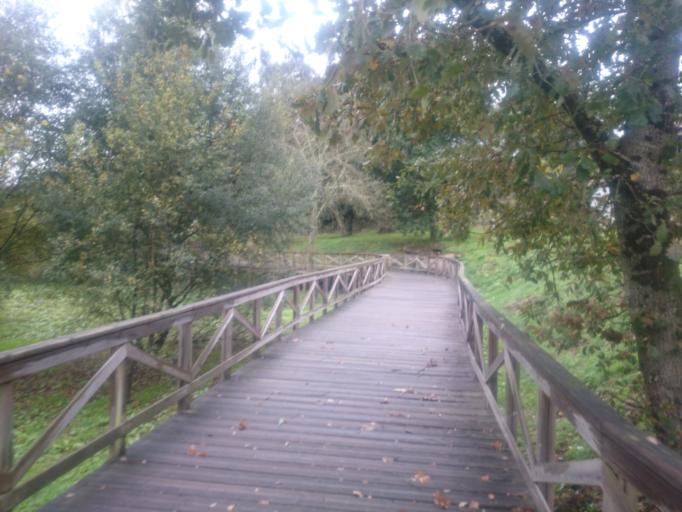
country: ES
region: Galicia
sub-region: Provincia de Ourense
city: Ribadavia
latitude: 42.2562
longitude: -8.1505
